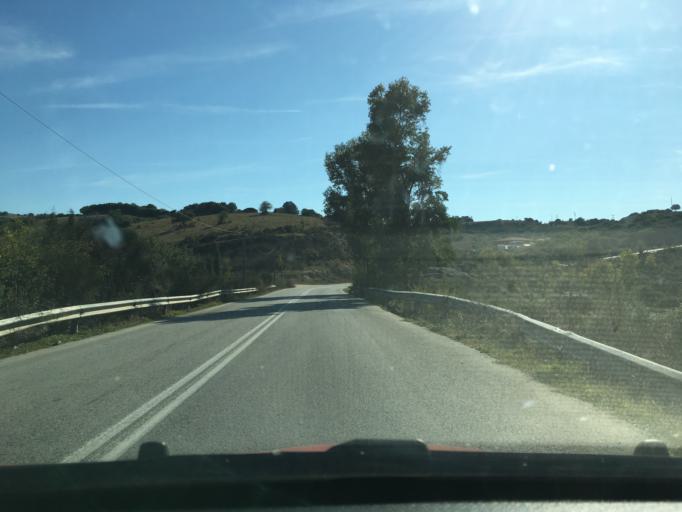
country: GR
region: Central Macedonia
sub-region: Nomos Chalkidikis
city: Ierissos
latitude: 40.3897
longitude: 23.8622
